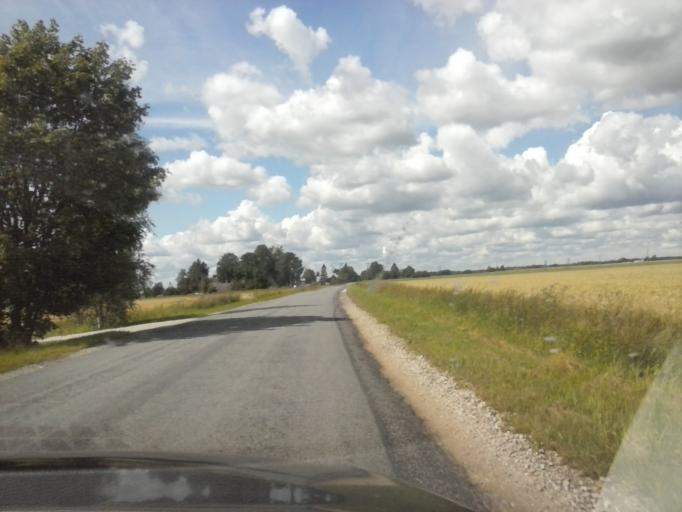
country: EE
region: Laeaene-Virumaa
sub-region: Rakke vald
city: Rakke
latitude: 59.0552
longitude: 26.3481
